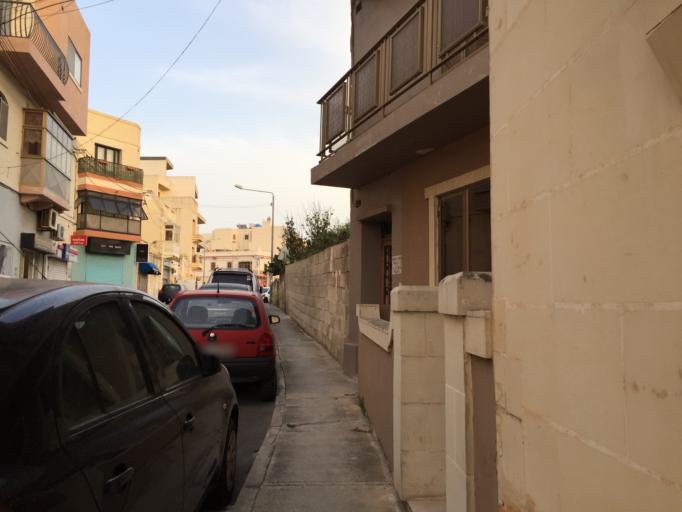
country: MT
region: Il-Fgura
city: Fgura
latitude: 35.8731
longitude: 14.5230
